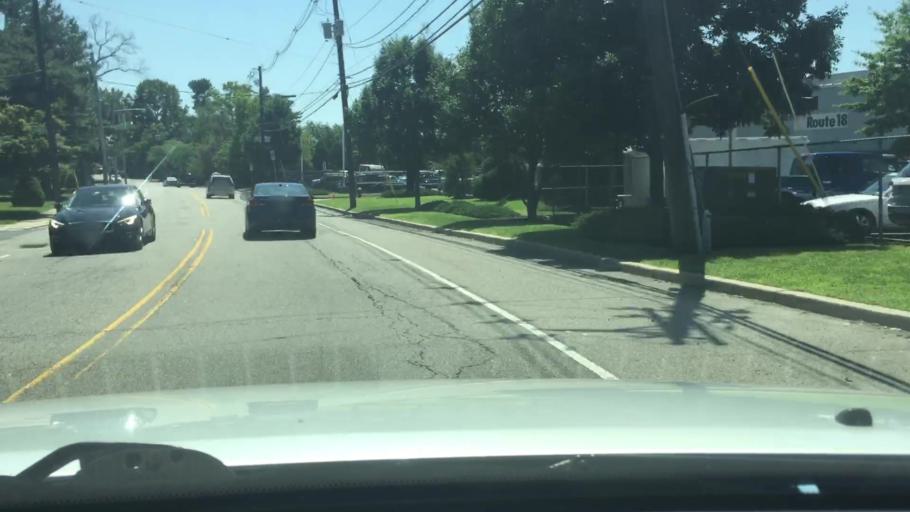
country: US
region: New Jersey
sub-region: Middlesex County
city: South River
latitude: 40.4488
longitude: -74.3953
